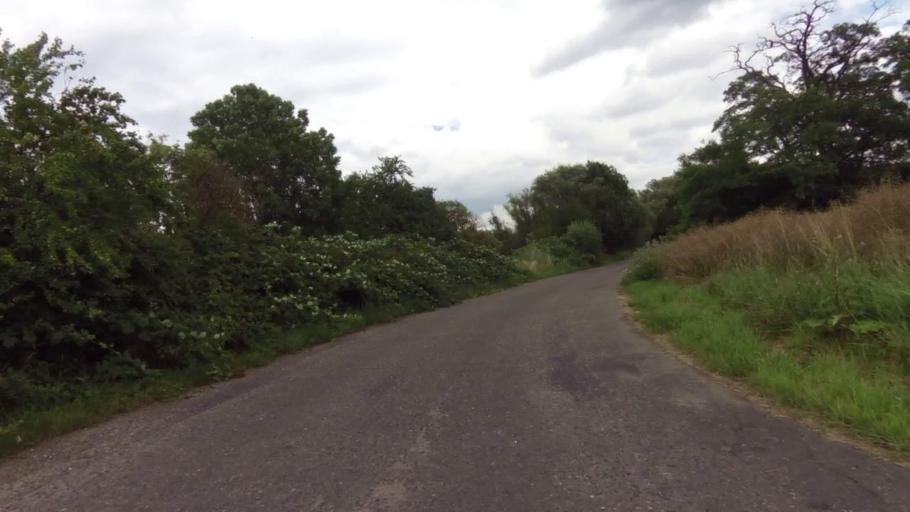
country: PL
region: West Pomeranian Voivodeship
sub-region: Powiat gryfinski
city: Moryn
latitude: 52.8693
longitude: 14.3300
